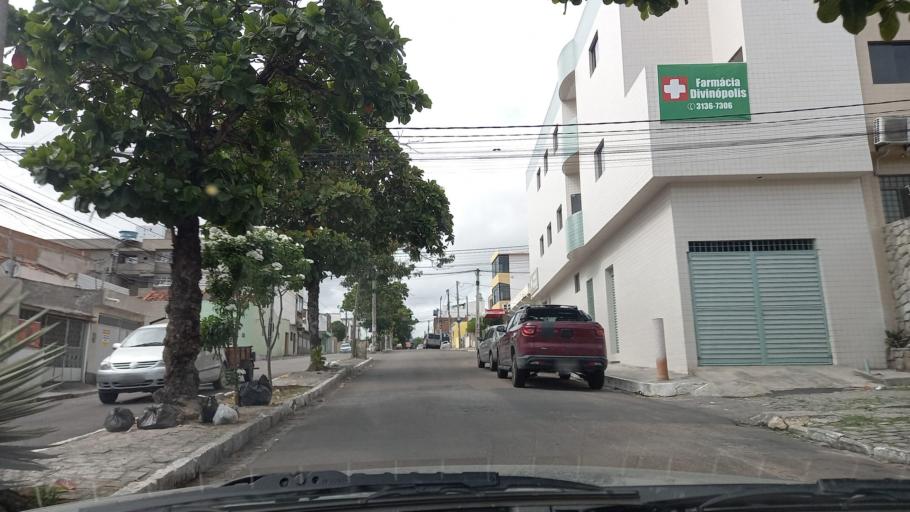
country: BR
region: Pernambuco
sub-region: Caruaru
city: Caruaru
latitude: -8.2786
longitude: -35.9777
